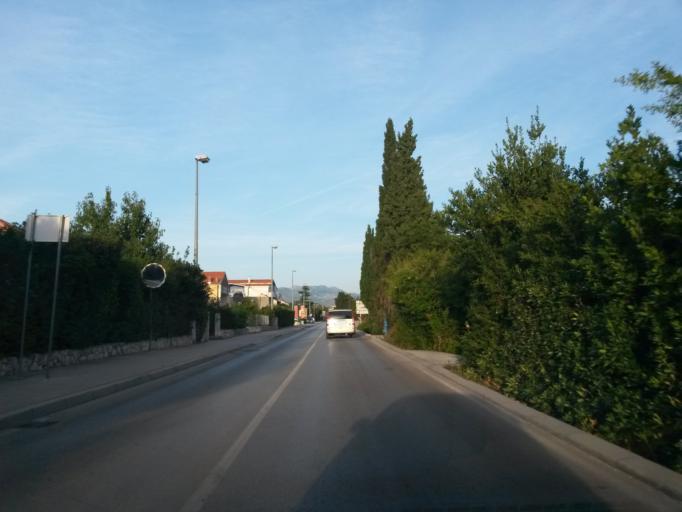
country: HR
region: Splitsko-Dalmatinska
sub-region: Grad Split
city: Split
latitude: 43.5535
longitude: 16.3671
